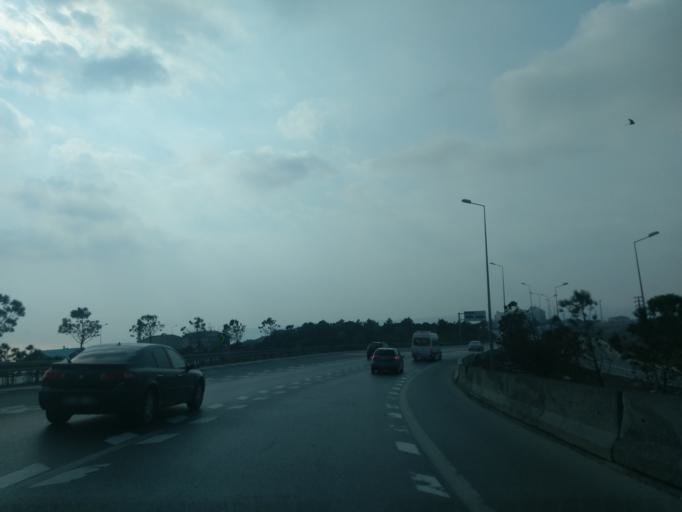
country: TR
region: Istanbul
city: Bueyuekcekmece
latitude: 41.0260
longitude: 28.6078
